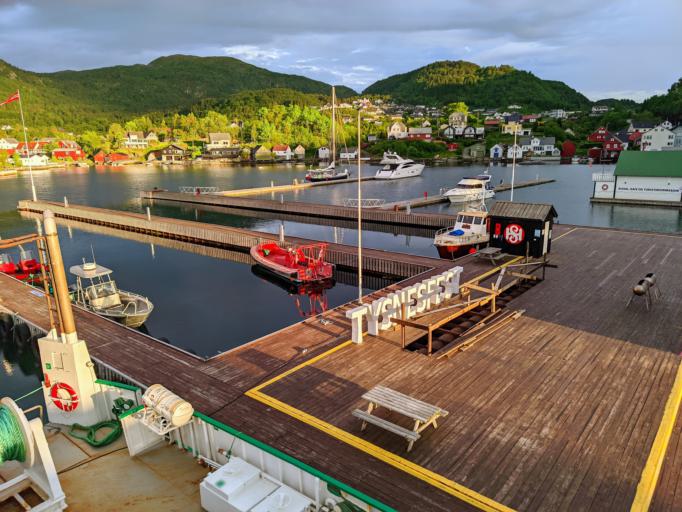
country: NO
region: Hordaland
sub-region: Tysnes
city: Uggdal
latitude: 60.0462
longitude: 5.5249
